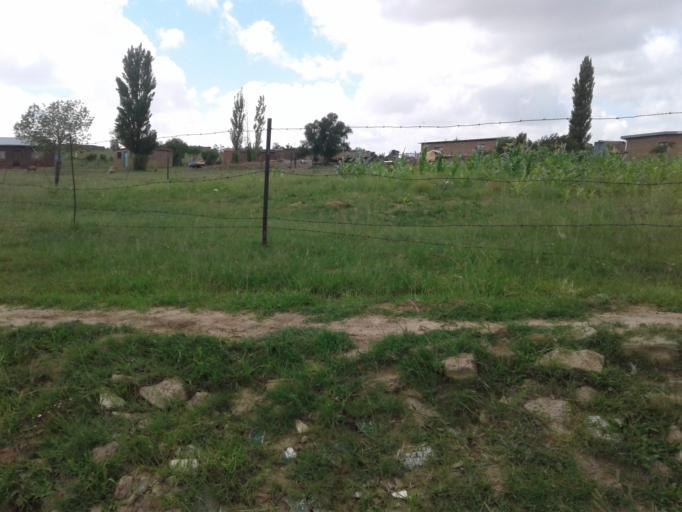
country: LS
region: Mafeteng
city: Mafeteng
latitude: -29.7496
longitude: 27.1117
